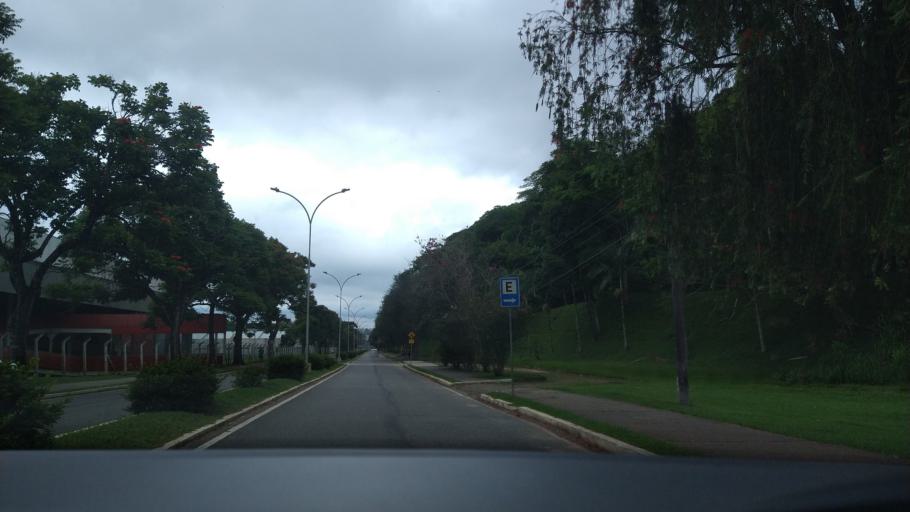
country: BR
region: Minas Gerais
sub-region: Vicosa
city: Vicosa
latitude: -20.7661
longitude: -42.8626
